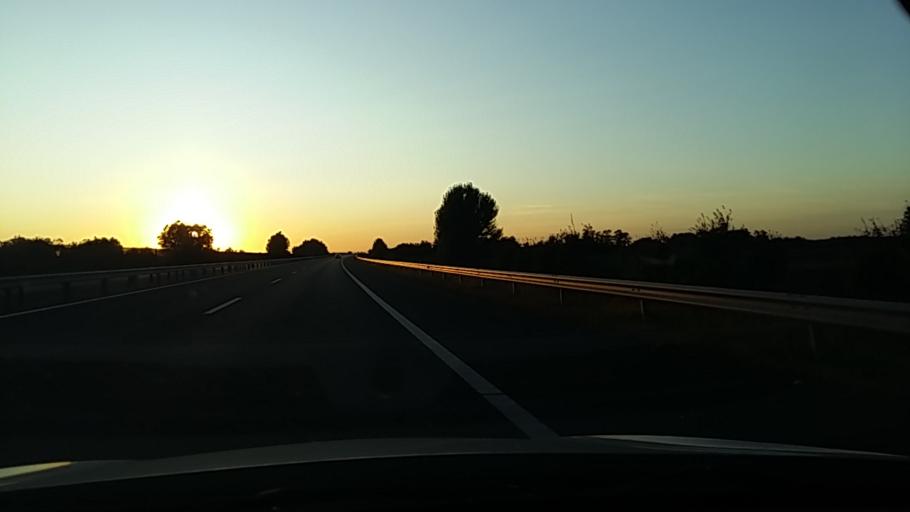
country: HU
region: Szabolcs-Szatmar-Bereg
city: Kalmanhaza
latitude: 47.8996
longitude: 21.5319
